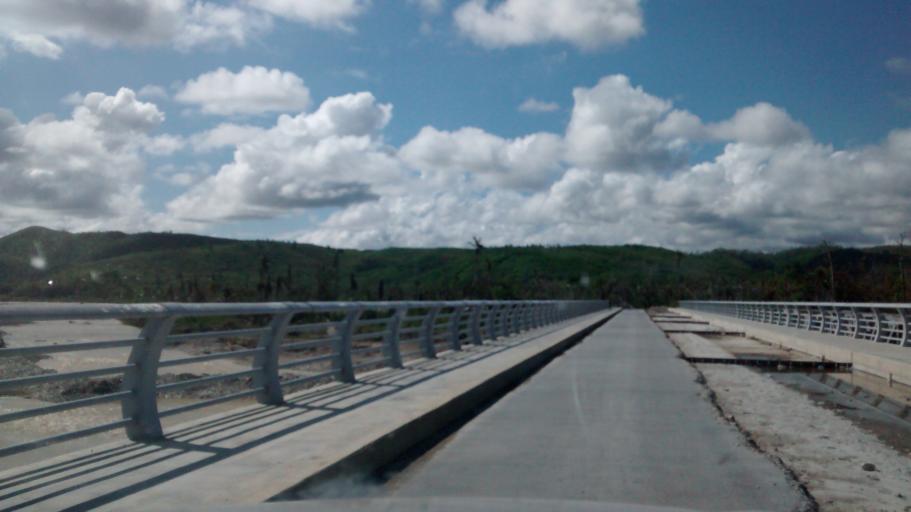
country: HT
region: Grandans
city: Jeremie
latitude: 18.6109
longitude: -74.0771
